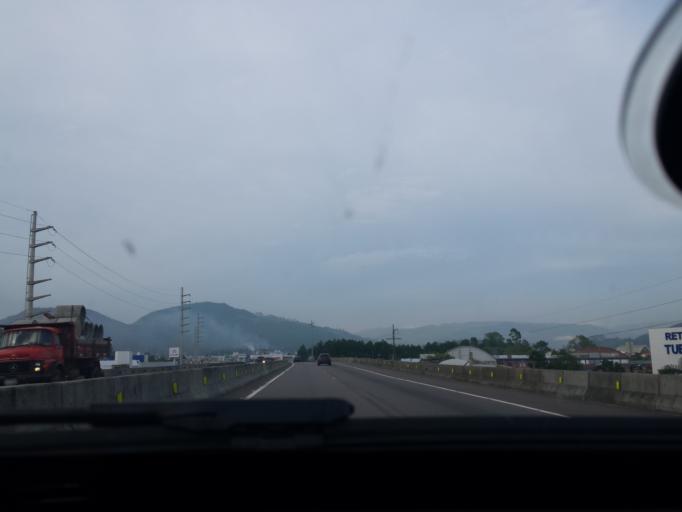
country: BR
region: Santa Catarina
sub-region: Tubarao
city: Tubarao
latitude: -28.4701
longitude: -49.0174
